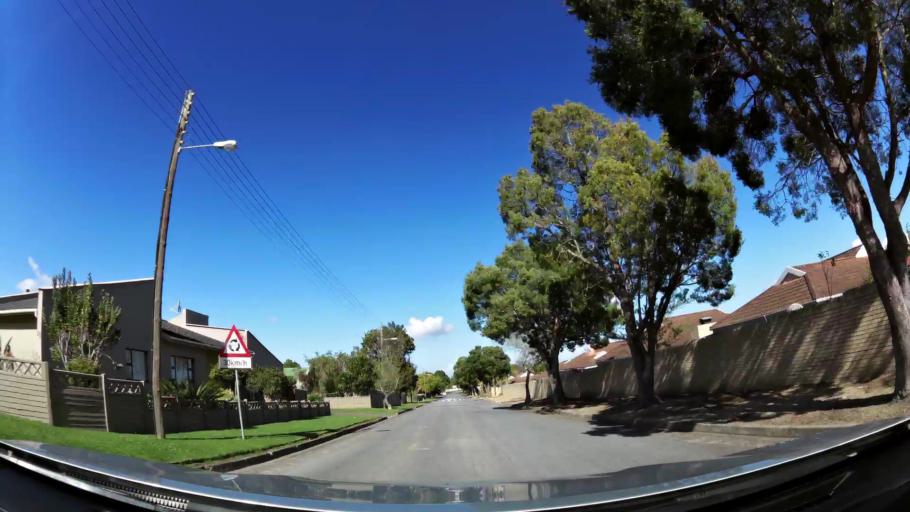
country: ZA
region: Western Cape
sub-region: Eden District Municipality
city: George
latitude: -33.9406
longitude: 22.4718
